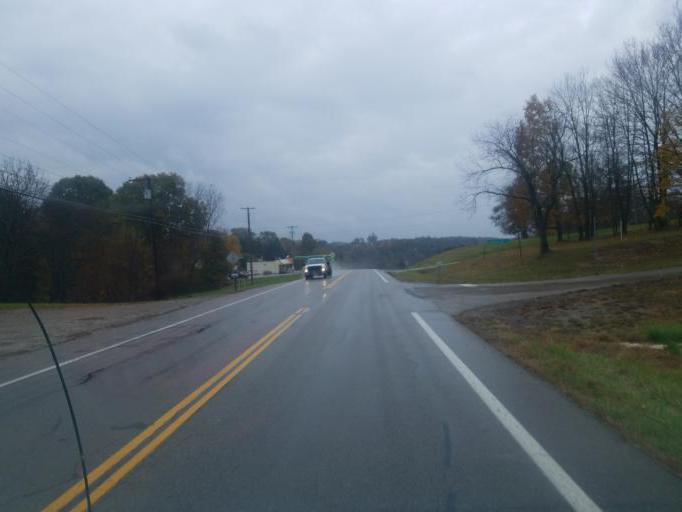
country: US
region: Ohio
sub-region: Muskingum County
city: Frazeysburg
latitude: 40.0273
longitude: -82.0998
